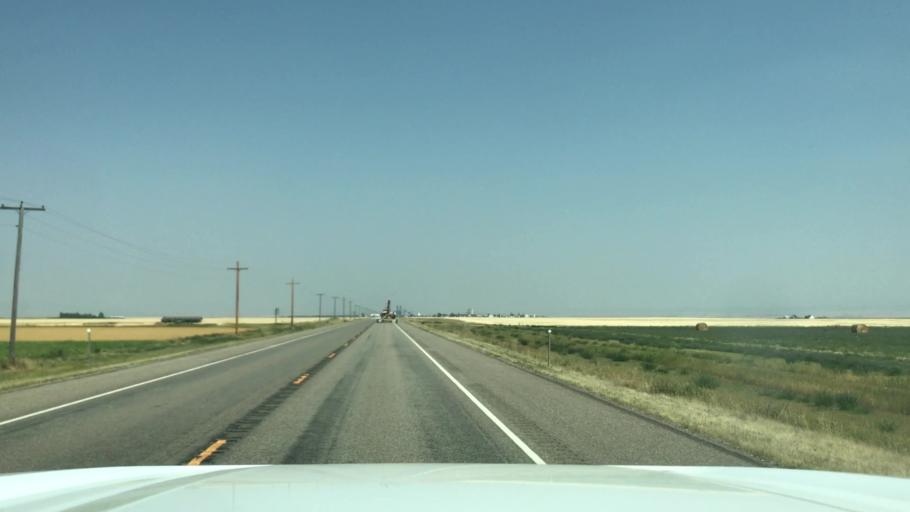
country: US
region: Montana
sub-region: Judith Basin County
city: Stanford
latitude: 47.0552
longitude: -109.9489
